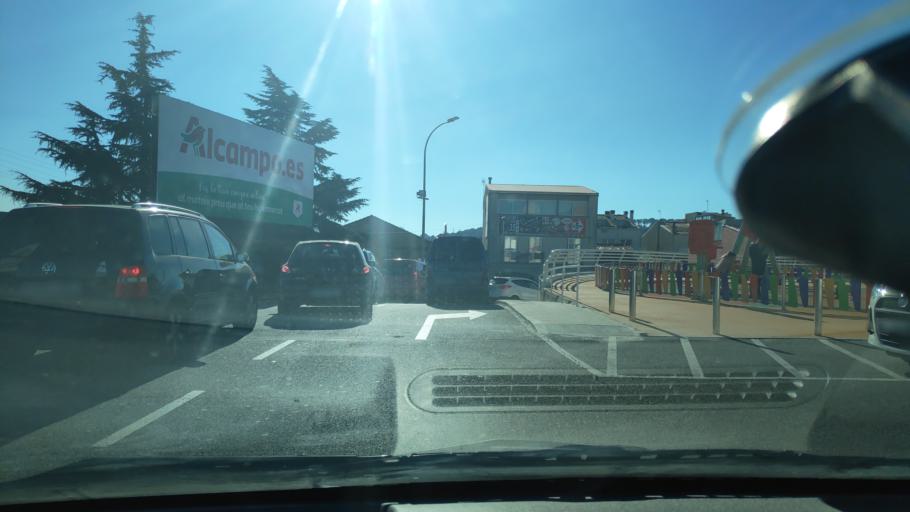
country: ES
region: Catalonia
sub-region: Provincia de Barcelona
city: Sant Quirze del Valles
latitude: 41.5284
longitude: 2.0906
